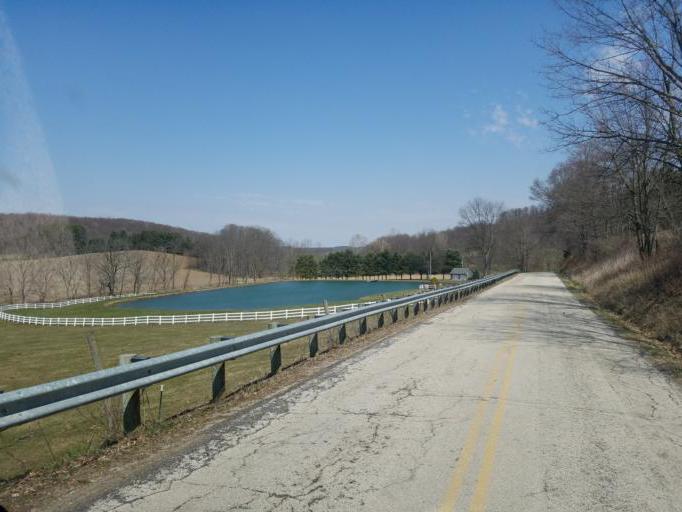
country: US
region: Ohio
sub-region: Ashland County
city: Loudonville
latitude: 40.6158
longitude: -82.1664
